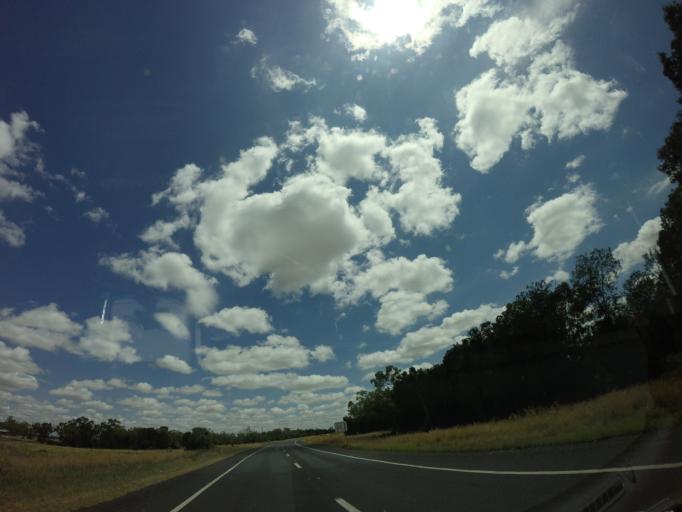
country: AU
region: New South Wales
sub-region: Moree Plains
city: Moree
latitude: -29.1776
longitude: 150.0095
